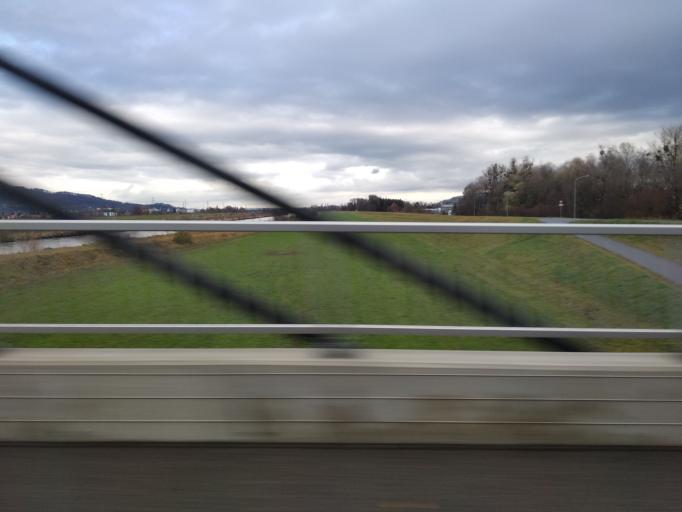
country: CH
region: Saint Gallen
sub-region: Wahlkreis Rheintal
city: Diepoldsau
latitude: 47.3902
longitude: 9.6476
